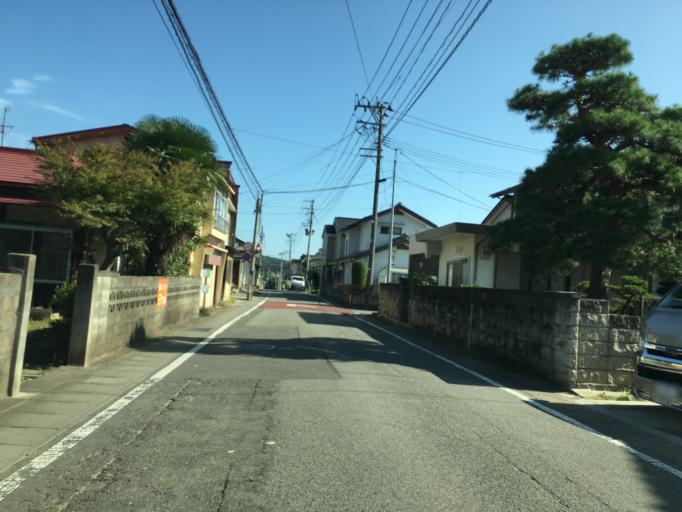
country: JP
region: Fukushima
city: Nihommatsu
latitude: 37.5813
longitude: 140.4197
